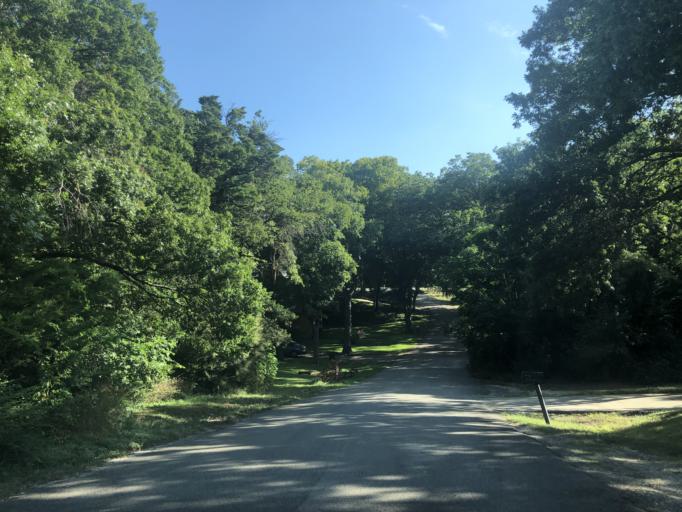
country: US
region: Texas
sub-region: Dallas County
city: Duncanville
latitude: 32.6623
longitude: -96.9214
